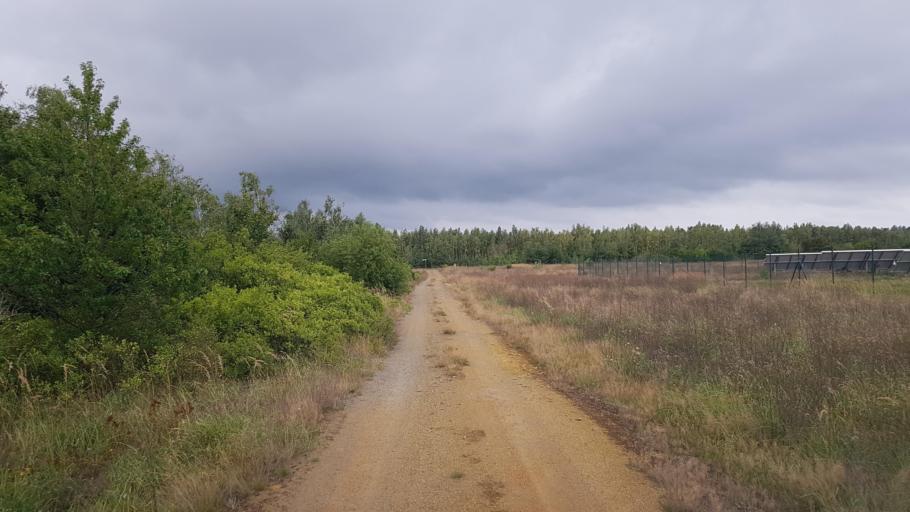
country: DE
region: Brandenburg
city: Finsterwalde
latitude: 51.5639
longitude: 13.7289
